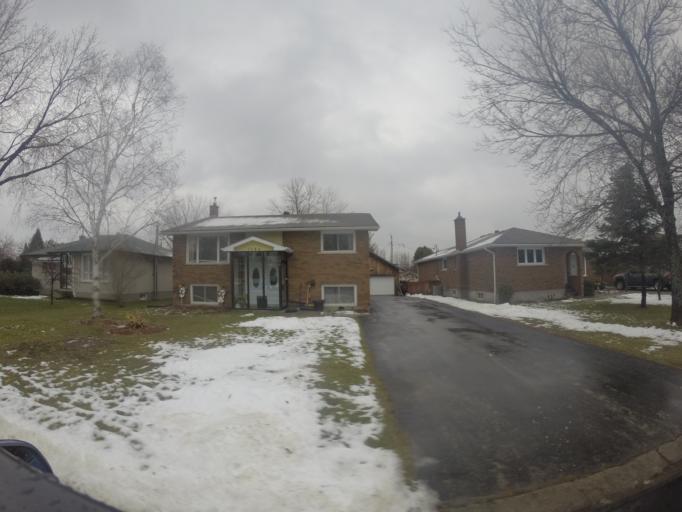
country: CA
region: Ontario
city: Greater Sudbury
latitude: 46.5255
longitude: -80.9355
